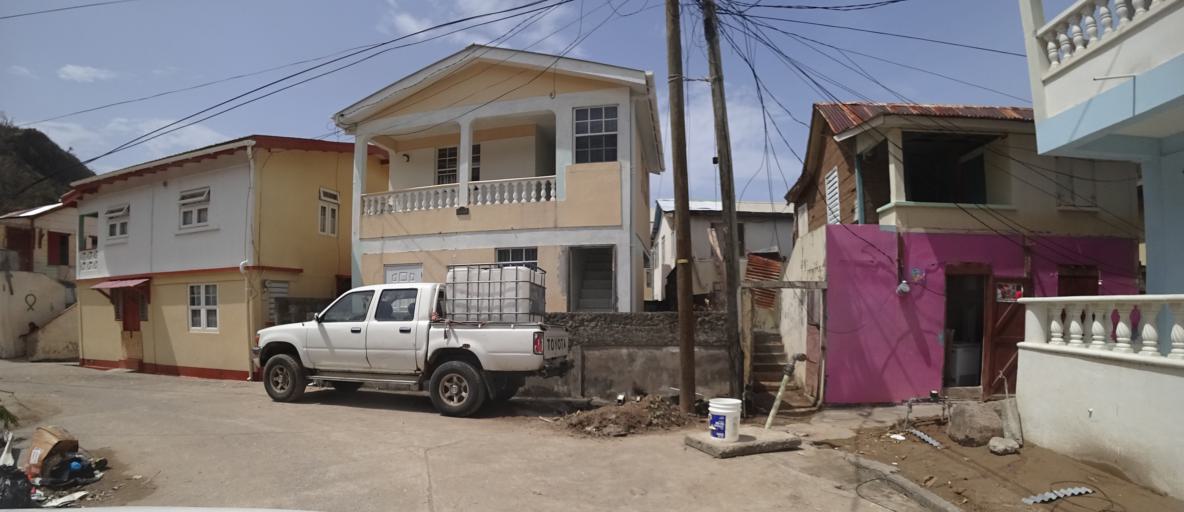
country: DM
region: Saint Peter
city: Colihaut
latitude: 15.4857
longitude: -61.4625
